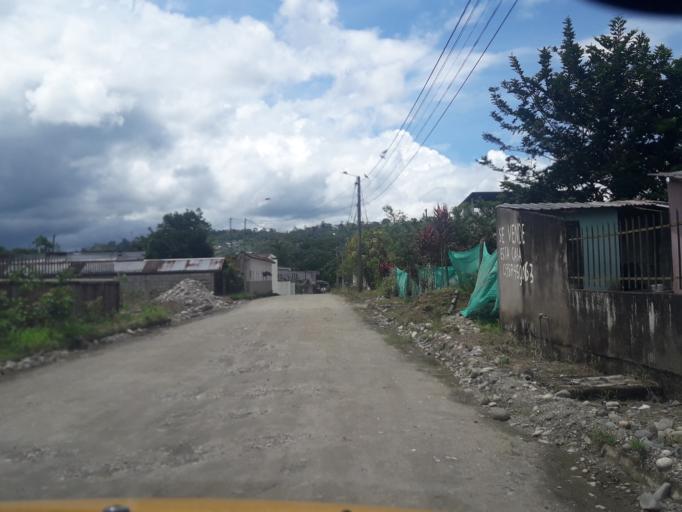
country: EC
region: Napo
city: Tena
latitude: -1.0033
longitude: -77.8193
